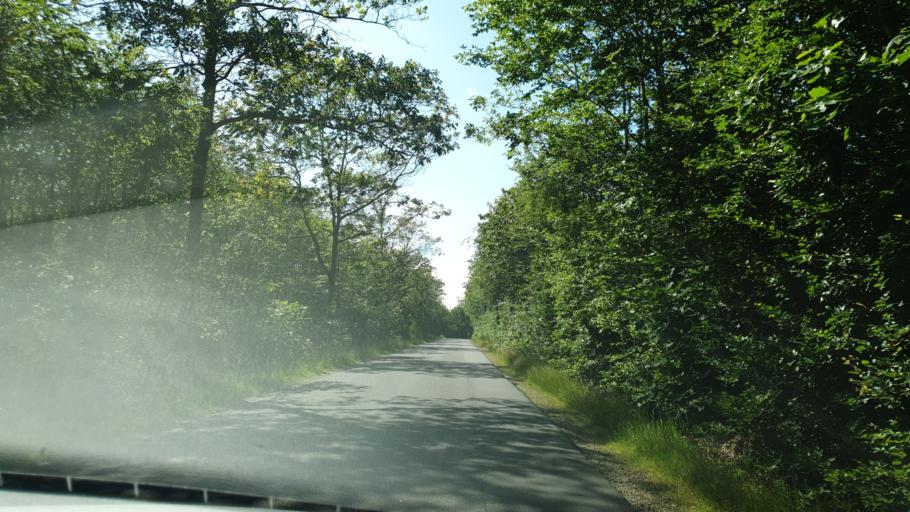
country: DK
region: Central Jutland
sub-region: Ringkobing-Skjern Kommune
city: Skjern
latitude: 55.9996
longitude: 8.4339
